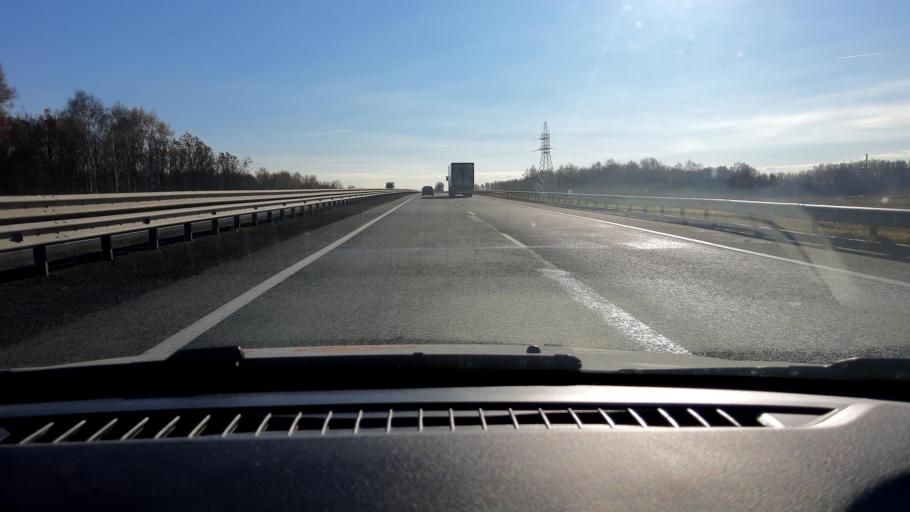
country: RU
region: Nizjnij Novgorod
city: Burevestnik
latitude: 56.1377
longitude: 43.7674
